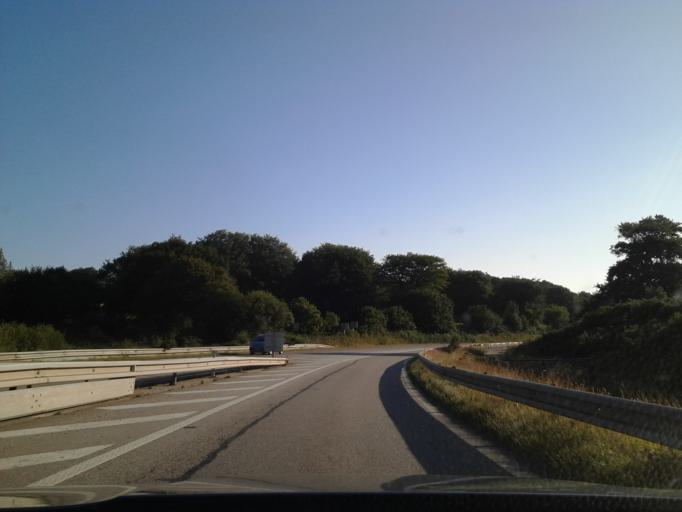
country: FR
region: Lower Normandy
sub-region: Departement de la Manche
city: La Glacerie
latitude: 49.6048
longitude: -1.5942
